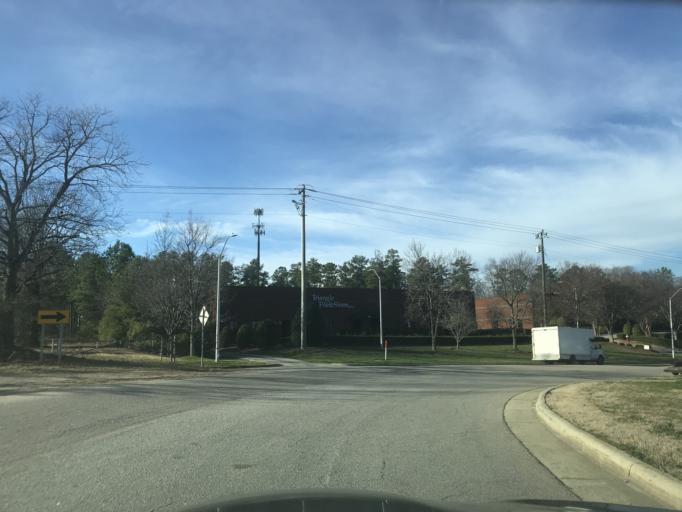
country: US
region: North Carolina
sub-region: Wake County
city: Cary
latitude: 35.7905
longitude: -78.7515
